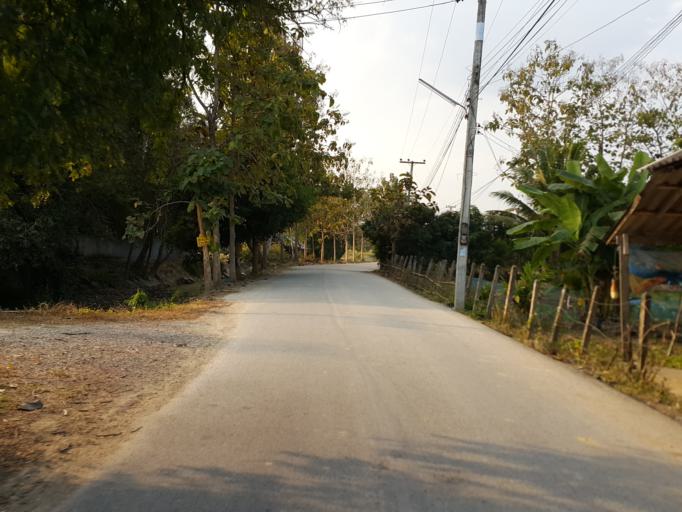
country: TH
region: Chiang Mai
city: San Sai
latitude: 18.8241
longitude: 99.0899
